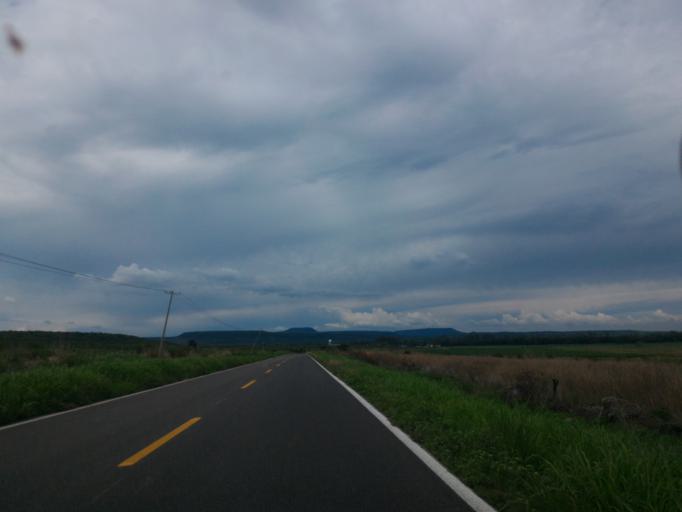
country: MX
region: Jalisco
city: San Diego de Alejandria
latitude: 20.8596
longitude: -101.9963
